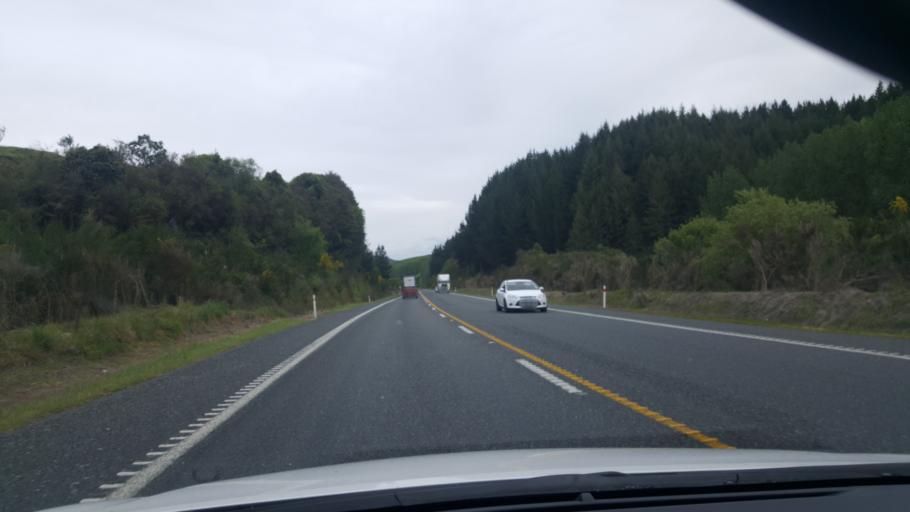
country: NZ
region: Bay of Plenty
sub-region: Rotorua District
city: Rotorua
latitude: -38.2888
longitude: 176.3512
